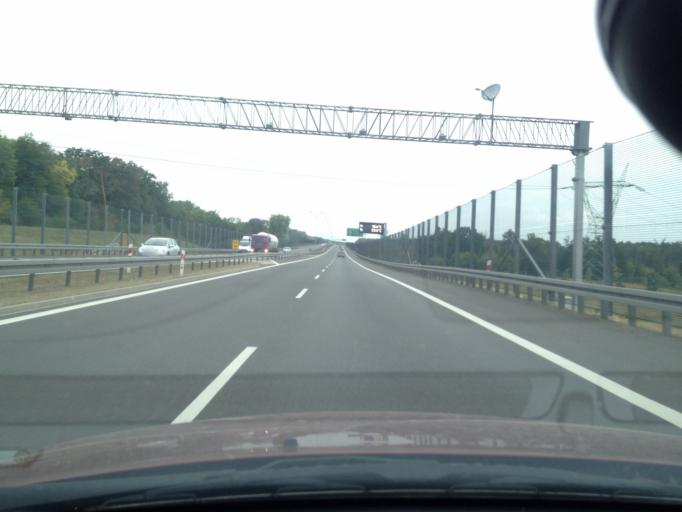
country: PL
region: Lubusz
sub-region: Powiat miedzyrzecki
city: Skwierzyna
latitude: 52.5812
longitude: 15.4610
